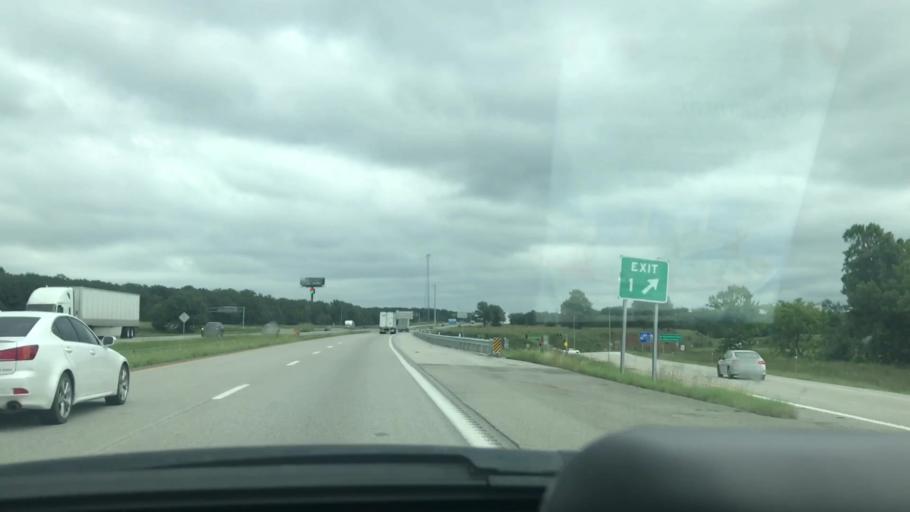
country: US
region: Kansas
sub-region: Cherokee County
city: Galena
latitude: 36.9972
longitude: -94.6147
